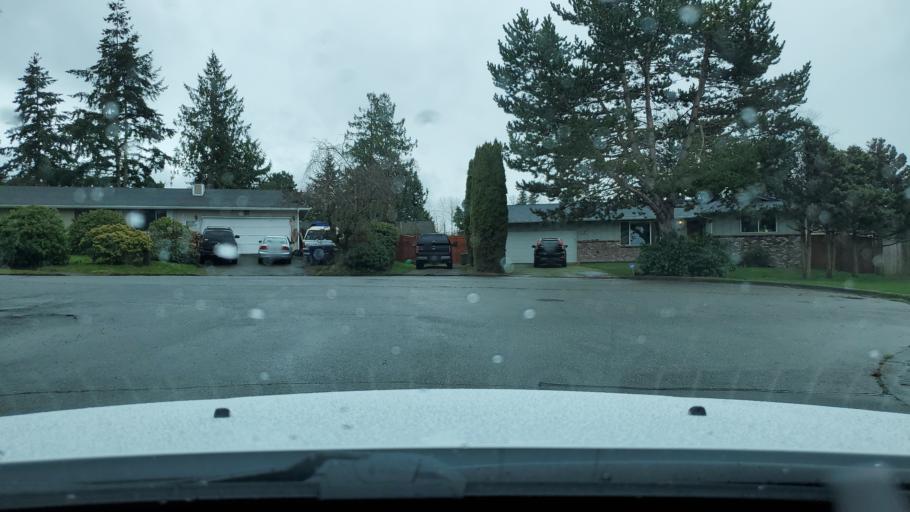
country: US
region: Washington
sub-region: Skagit County
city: Mount Vernon
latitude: 48.4417
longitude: -122.3169
